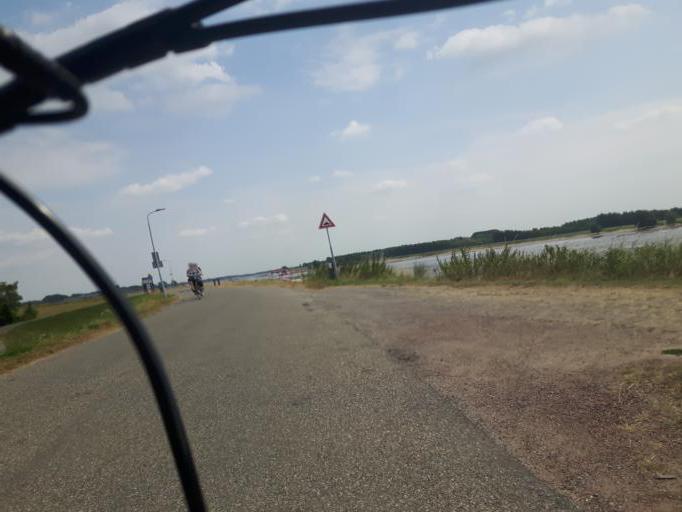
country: NL
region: Gelderland
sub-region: Gemeente Zaltbommel
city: Nederhemert
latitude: 51.8182
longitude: 5.1575
